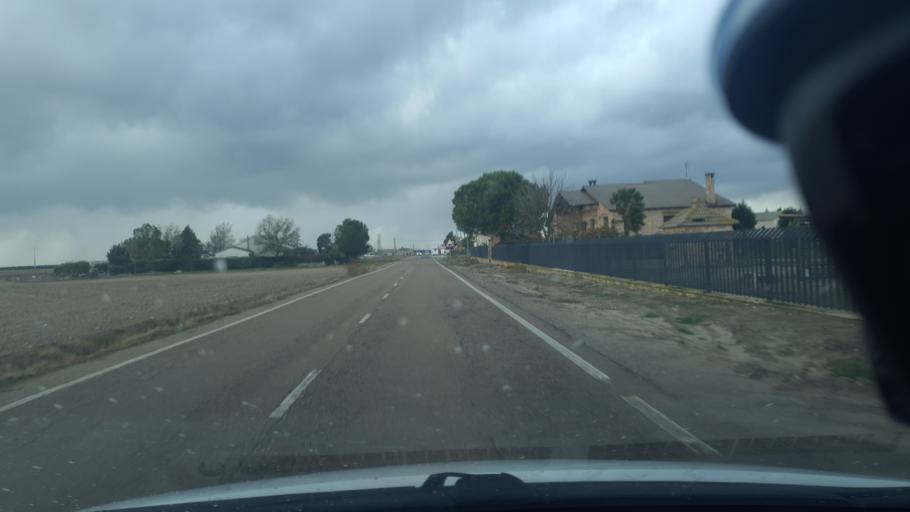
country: ES
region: Castille and Leon
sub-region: Provincia de Segovia
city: Sanchonuno
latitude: 41.3088
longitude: -4.3626
